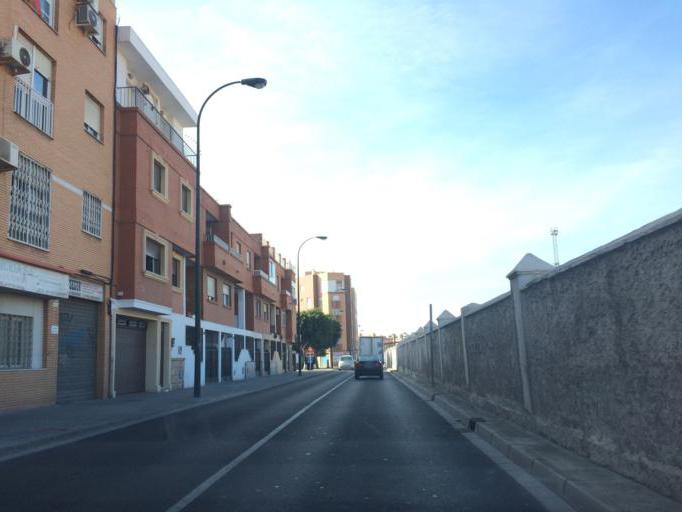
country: ES
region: Andalusia
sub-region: Provincia de Almeria
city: Almeria
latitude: 36.8352
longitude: -2.4521
